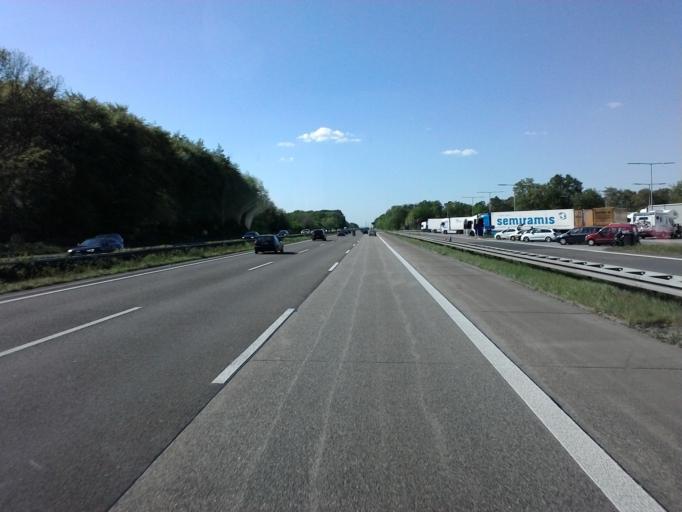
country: DE
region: North Rhine-Westphalia
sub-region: Regierungsbezirk Dusseldorf
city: Ratingen
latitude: 51.3257
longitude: 6.8909
